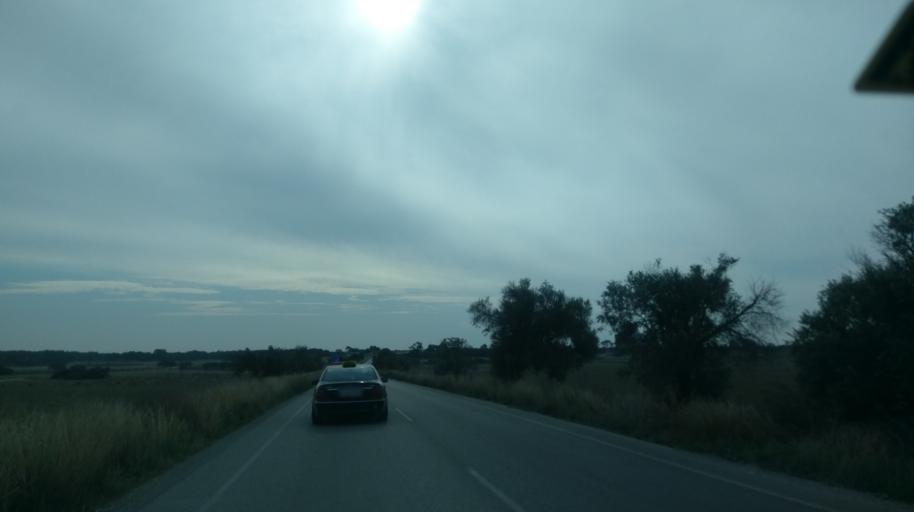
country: CY
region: Ammochostos
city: Leonarisso
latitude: 35.4389
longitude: 34.1365
